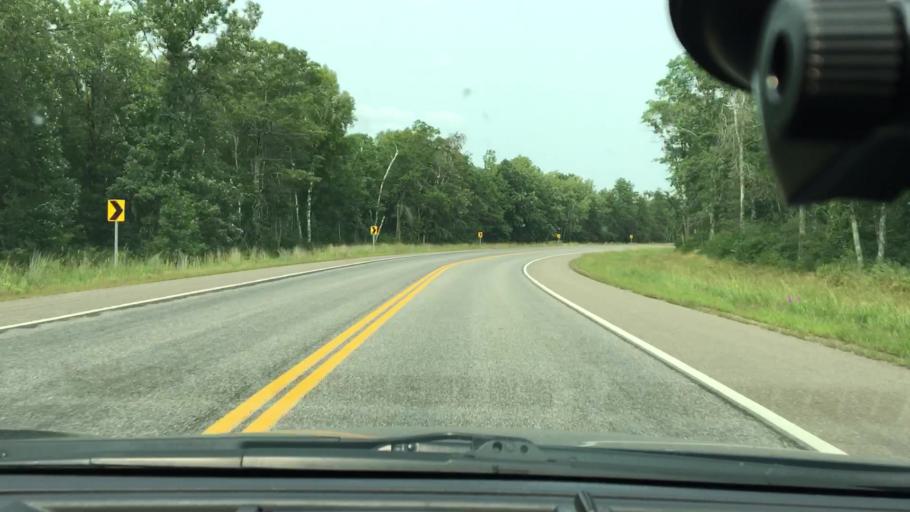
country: US
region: Minnesota
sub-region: Crow Wing County
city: Cross Lake
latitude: 46.6991
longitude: -94.0654
